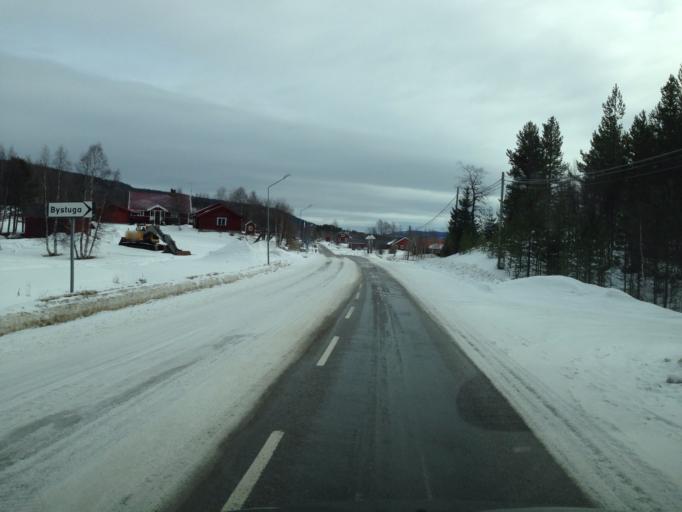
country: SE
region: Jaemtland
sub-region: Harjedalens Kommun
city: Sveg
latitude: 62.1128
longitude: 13.2650
